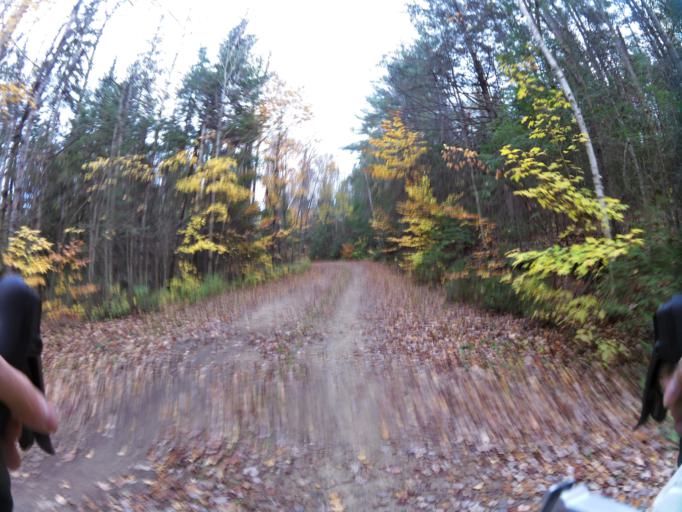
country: CA
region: Quebec
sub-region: Outaouais
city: Wakefield
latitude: 45.6140
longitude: -76.0192
